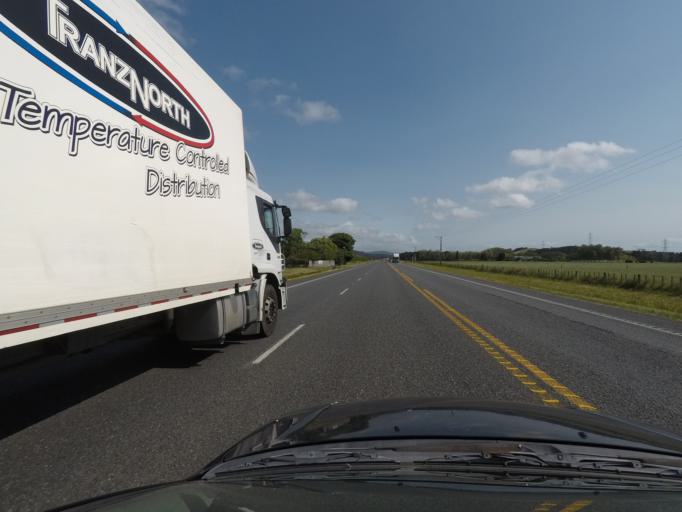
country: NZ
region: Northland
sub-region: Whangarei
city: Ruakaka
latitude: -36.0176
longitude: 174.4185
